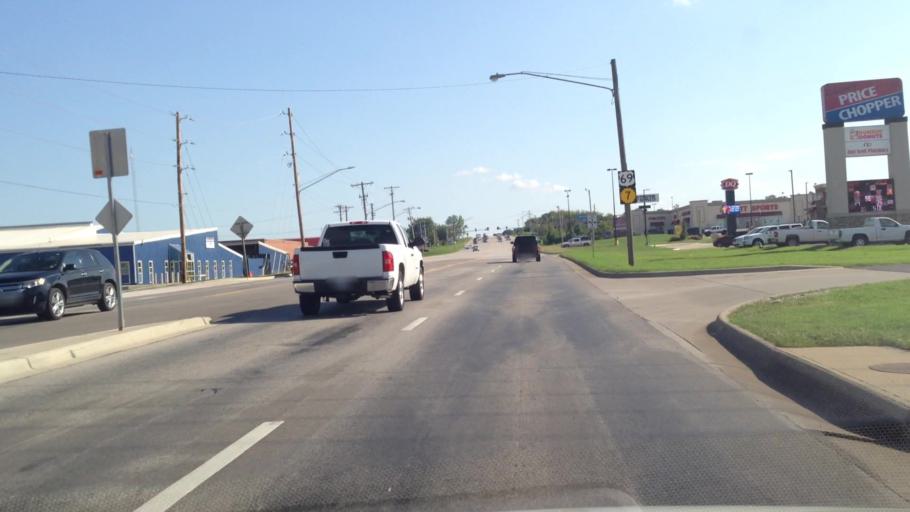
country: US
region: Kansas
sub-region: Bourbon County
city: Fort Scott
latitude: 37.8125
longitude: -94.7055
